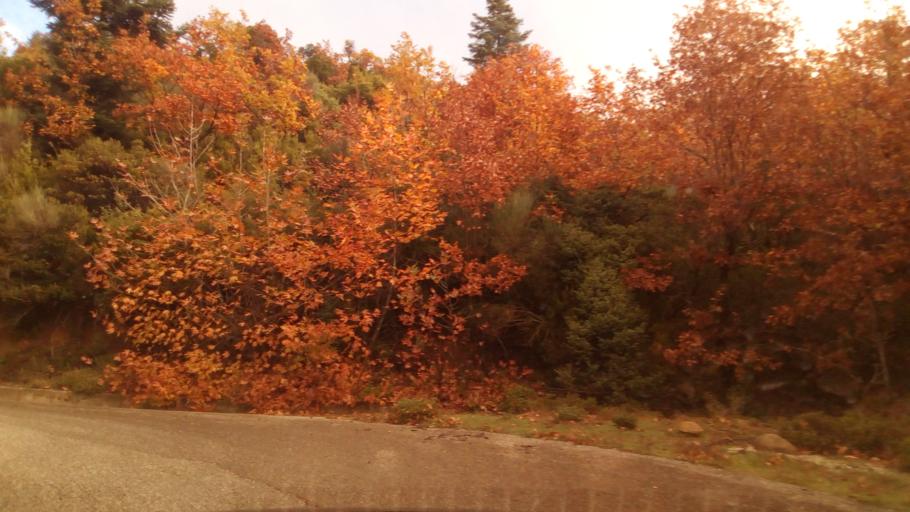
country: GR
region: West Greece
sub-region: Nomos Aitolias kai Akarnanias
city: Nafpaktos
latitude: 38.5457
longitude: 21.9261
